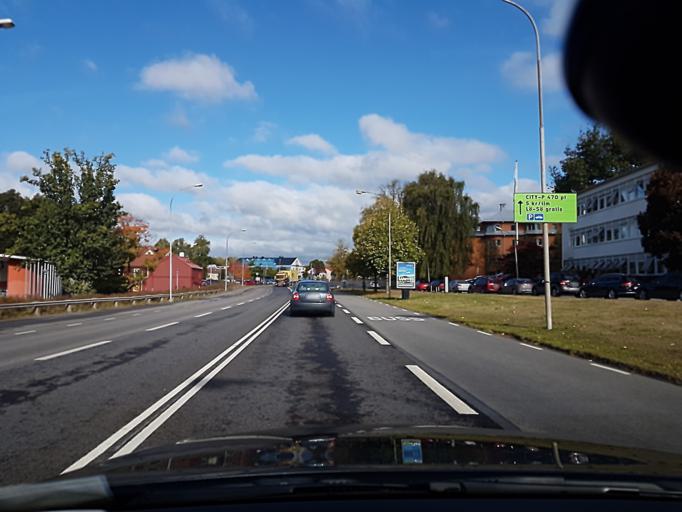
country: SE
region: Kronoberg
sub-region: Vaxjo Kommun
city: Vaexjoe
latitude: 56.8764
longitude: 14.8152
